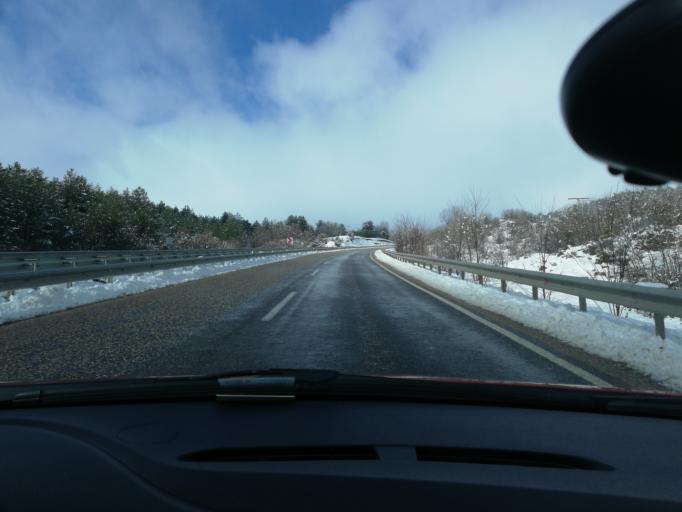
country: TR
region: Kastamonu
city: Ihsangazi
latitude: 41.3050
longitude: 33.5827
